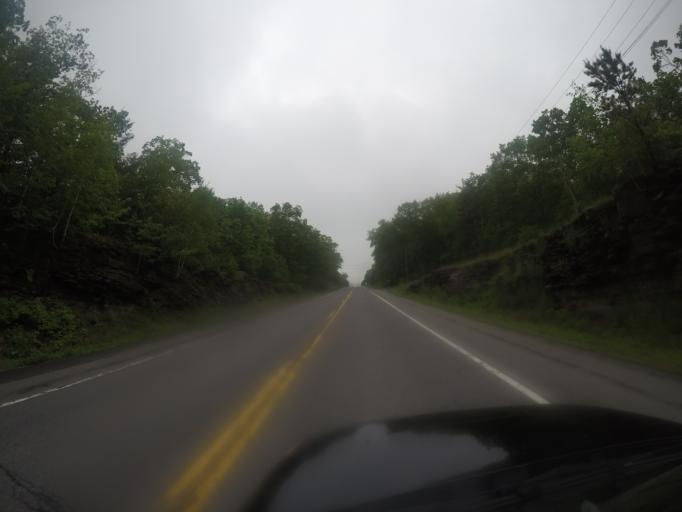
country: US
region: New York
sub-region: Ulster County
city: West Hurley
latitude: 41.9989
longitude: -74.1127
